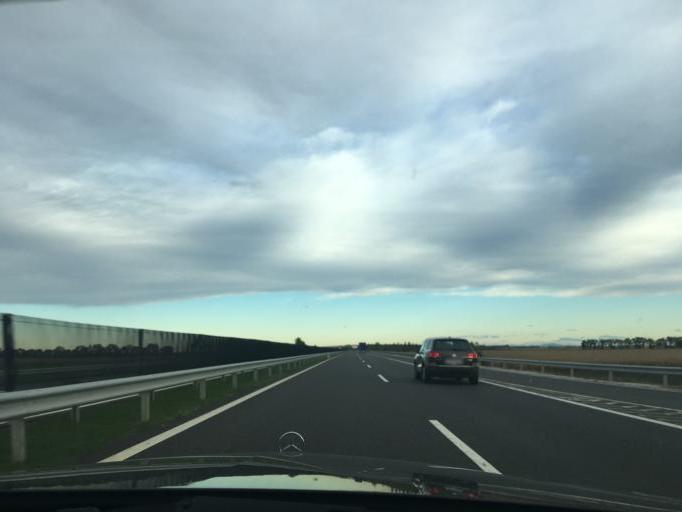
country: HU
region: Hajdu-Bihar
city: Hajduboszormeny
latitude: 47.7024
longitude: 21.4355
